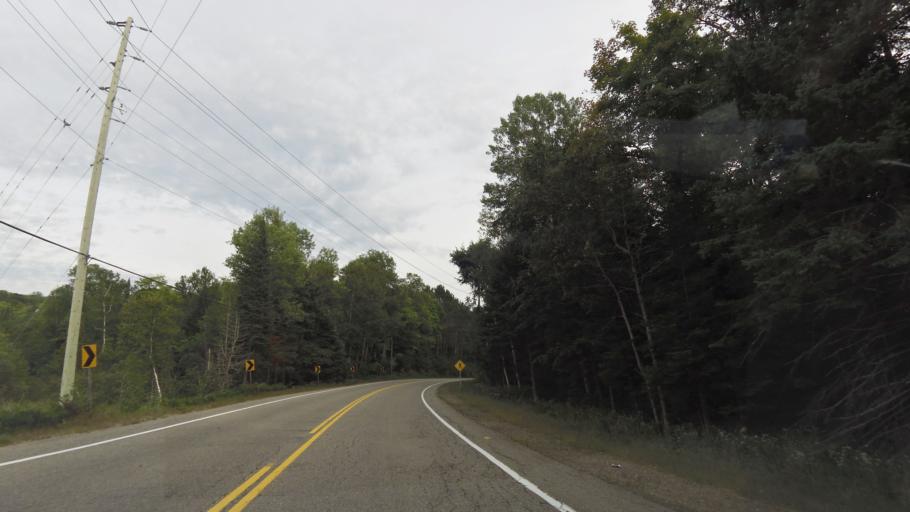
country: CA
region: Ontario
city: Bancroft
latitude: 45.0260
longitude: -78.3839
